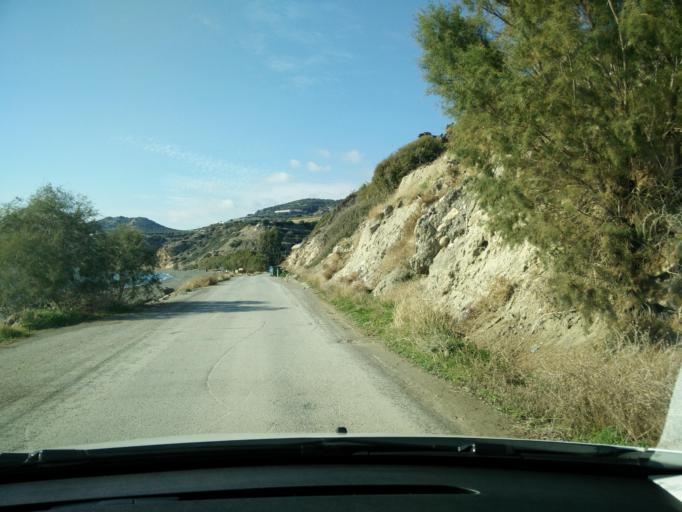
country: GR
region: Crete
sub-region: Nomos Lasithiou
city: Gra Liyia
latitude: 34.9906
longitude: 25.5370
